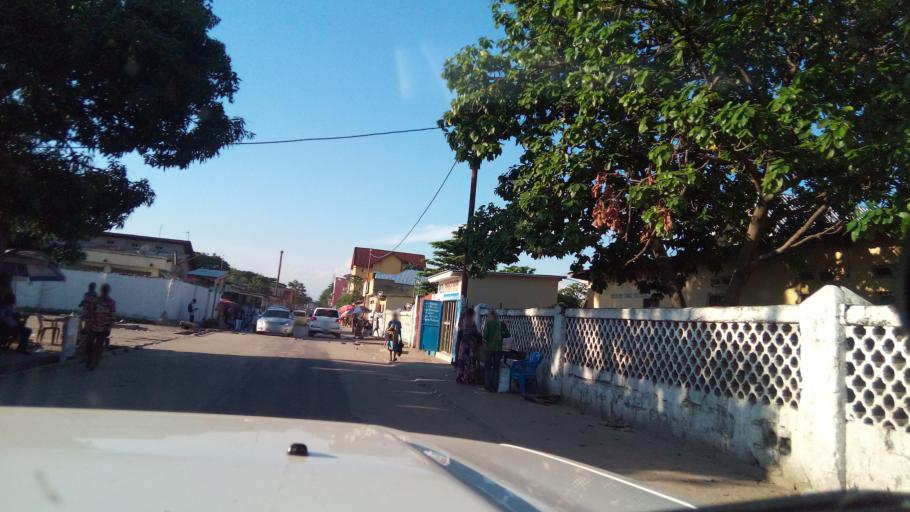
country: CD
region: Kinshasa
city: Kinshasa
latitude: -4.3415
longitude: 15.2677
